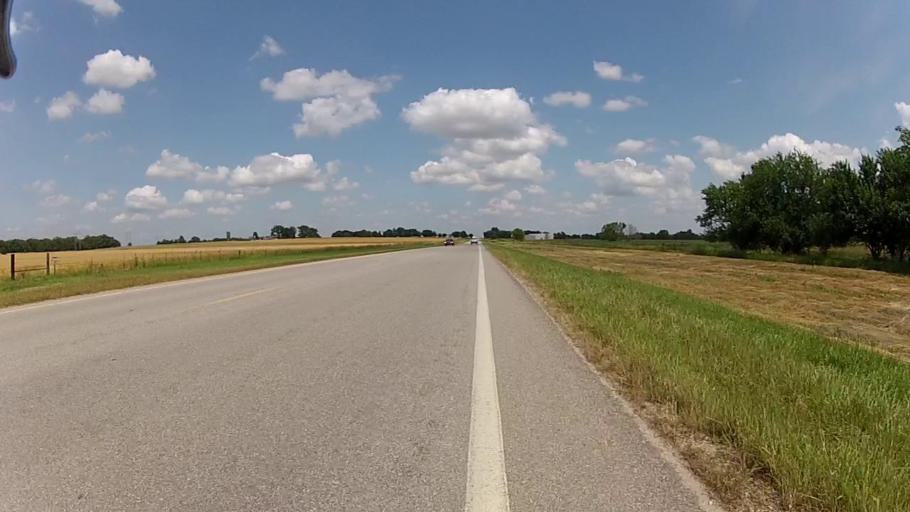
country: US
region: Kansas
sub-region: Labette County
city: Altamont
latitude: 37.1938
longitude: -95.2558
